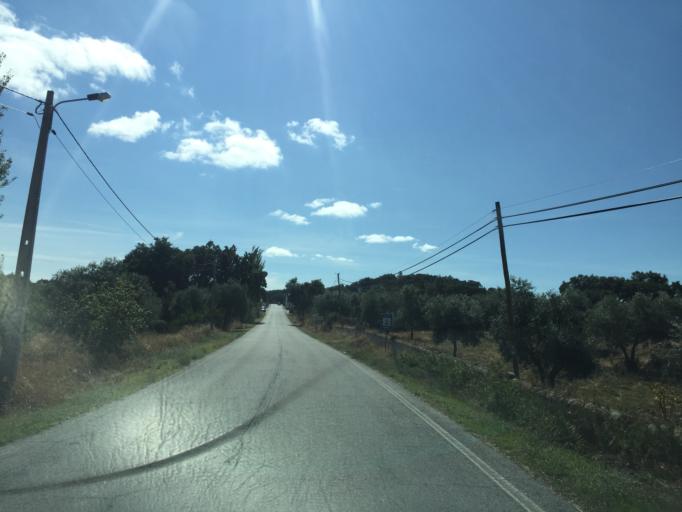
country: PT
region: Portalegre
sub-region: Marvao
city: Marvao
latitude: 39.4367
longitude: -7.3649
